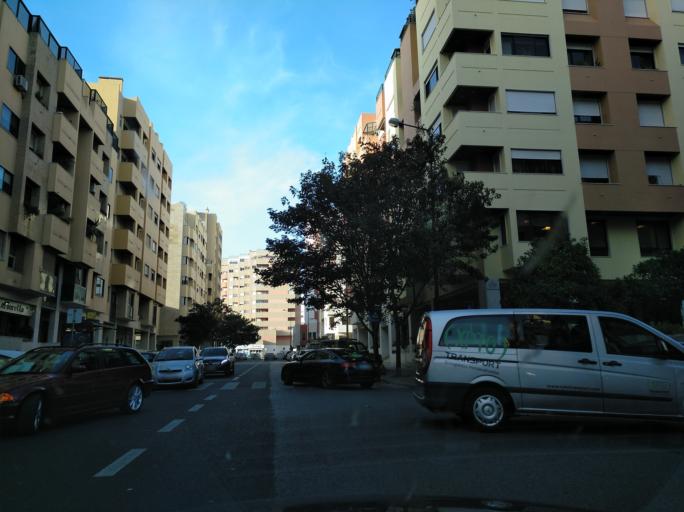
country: PT
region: Lisbon
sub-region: Odivelas
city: Pontinha
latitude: 38.7612
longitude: -9.1797
